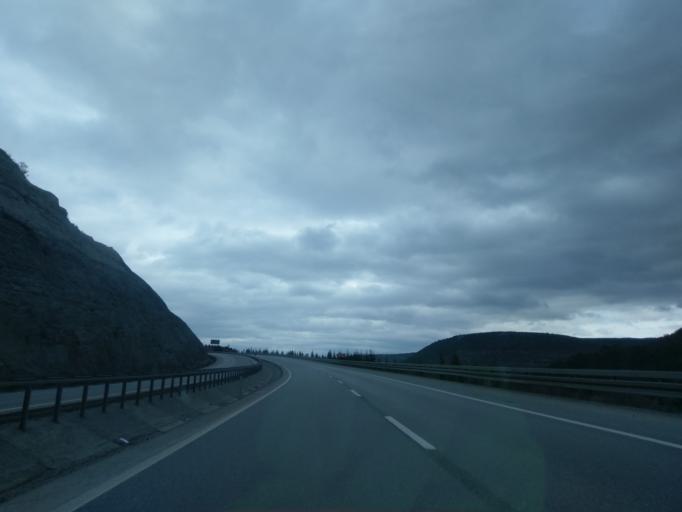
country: TR
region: Kuetahya
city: Sabuncu
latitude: 39.5848
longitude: 30.1284
